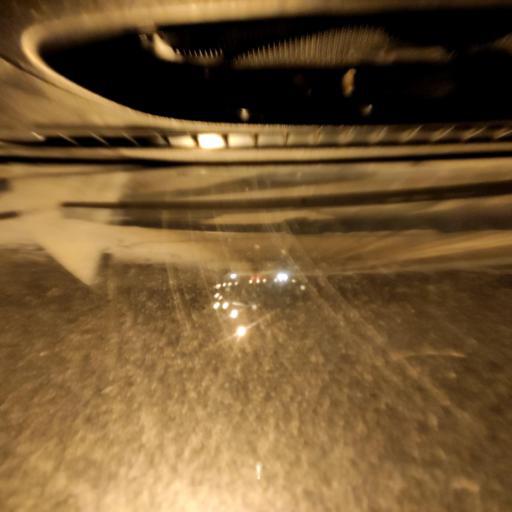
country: RU
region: Samara
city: Zhigulevsk
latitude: 53.4959
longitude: 49.5066
